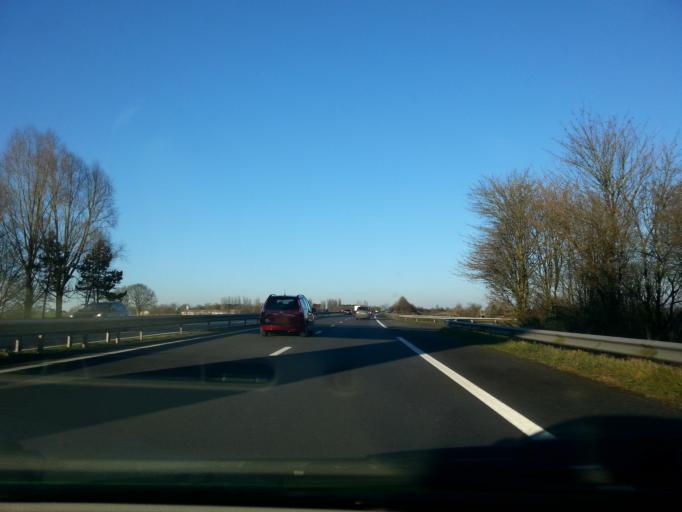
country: FR
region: Pays de la Loire
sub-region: Departement de la Sarthe
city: Noyen-sur-Sarthe
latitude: 47.8793
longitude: -0.1165
